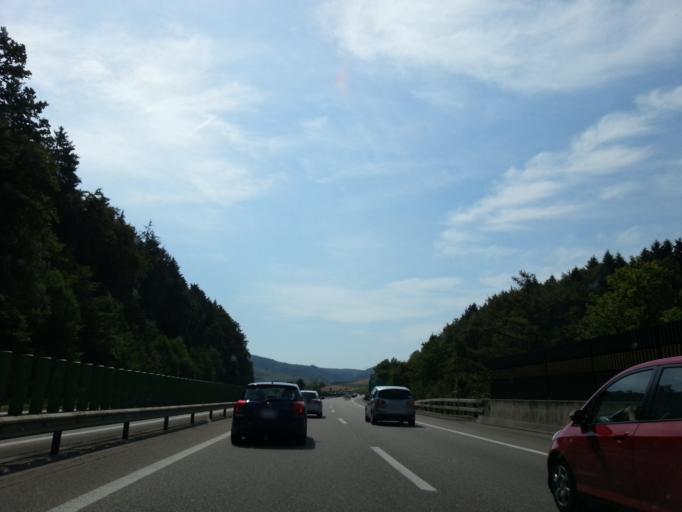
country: CH
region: Basel-Landschaft
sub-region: Bezirk Liestal
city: Arisdorf
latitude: 47.5226
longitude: 7.7516
